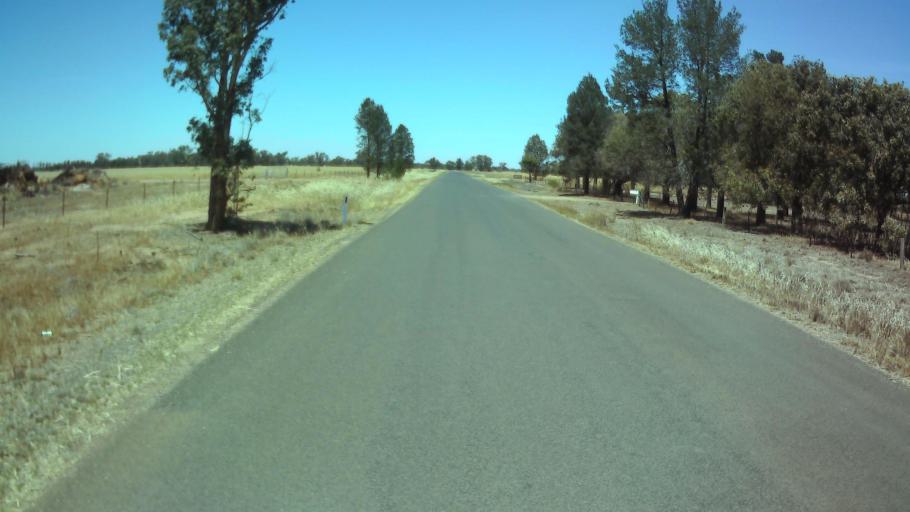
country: AU
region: New South Wales
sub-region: Weddin
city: Grenfell
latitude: -34.0316
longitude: 147.7907
